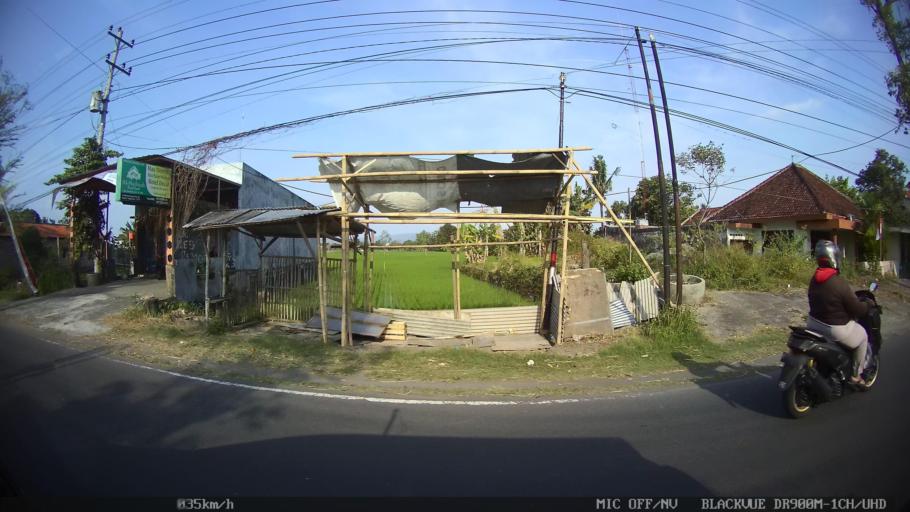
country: ID
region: Daerah Istimewa Yogyakarta
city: Bantul
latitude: -7.8939
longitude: 110.3247
